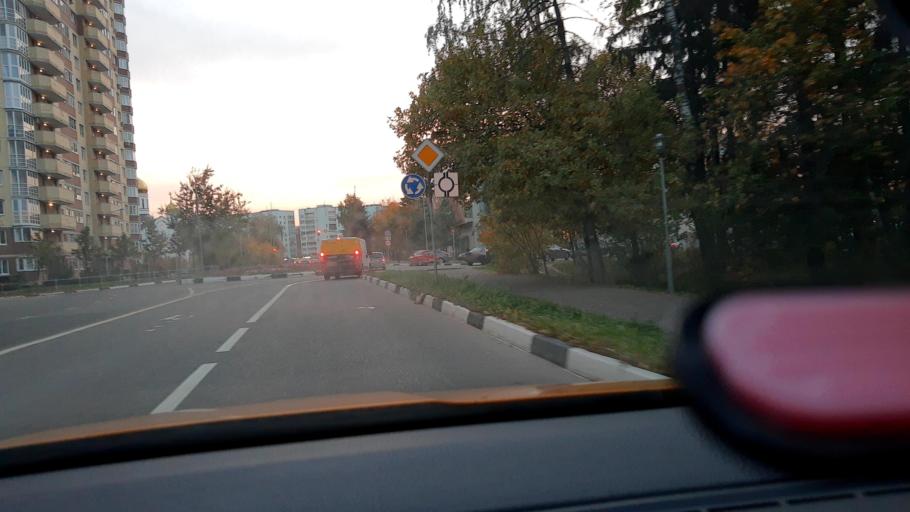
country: RU
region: Moskovskaya
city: Krasnoznamensk
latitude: 55.6018
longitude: 37.0466
